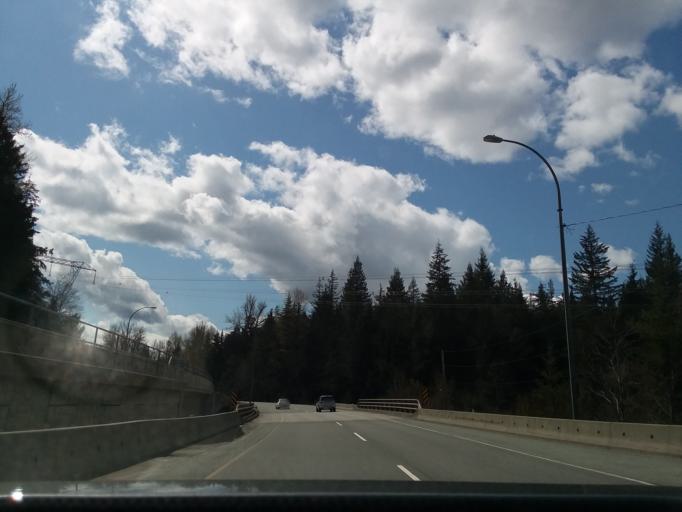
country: CA
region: British Columbia
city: Whistler
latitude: 49.9705
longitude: -123.1453
